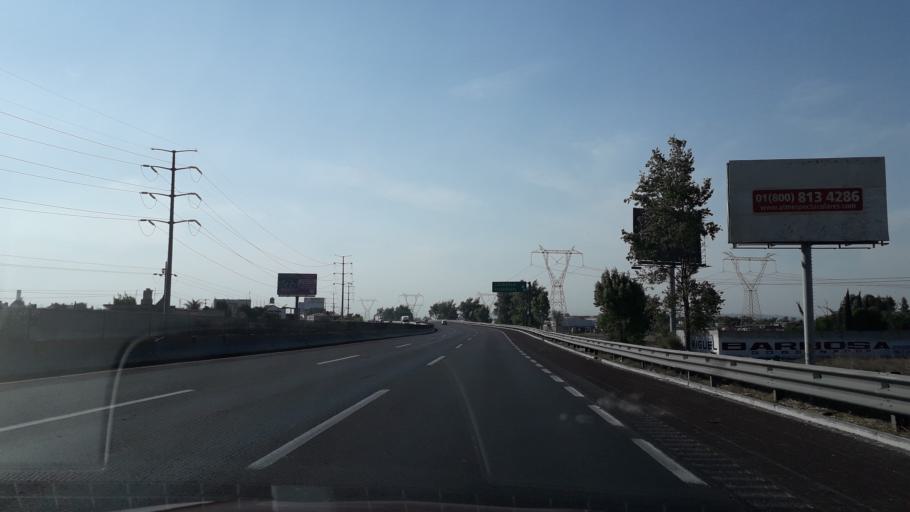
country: MX
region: Puebla
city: San Miguel Xoxtla
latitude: 19.1673
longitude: -98.2993
